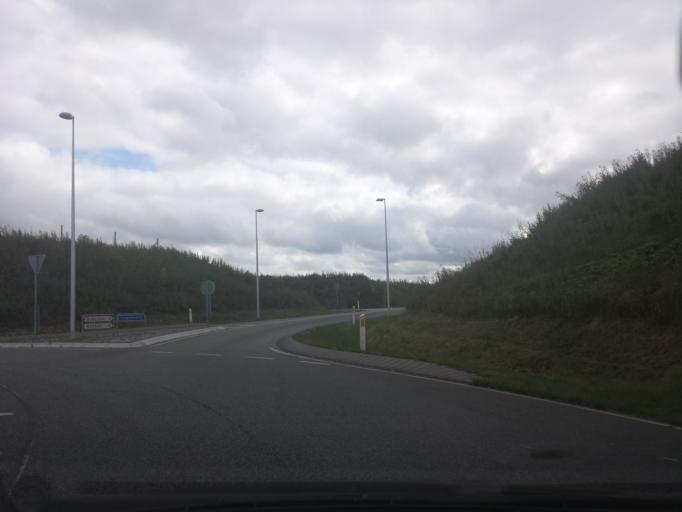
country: DK
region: South Denmark
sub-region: Sonderborg Kommune
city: Grasten
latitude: 54.9509
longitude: 9.6370
